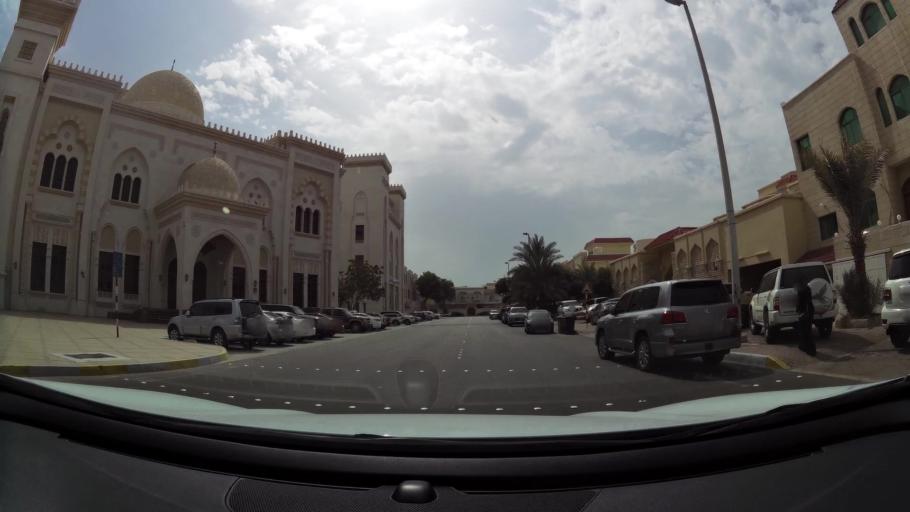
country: AE
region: Abu Dhabi
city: Abu Dhabi
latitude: 24.4682
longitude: 54.3599
